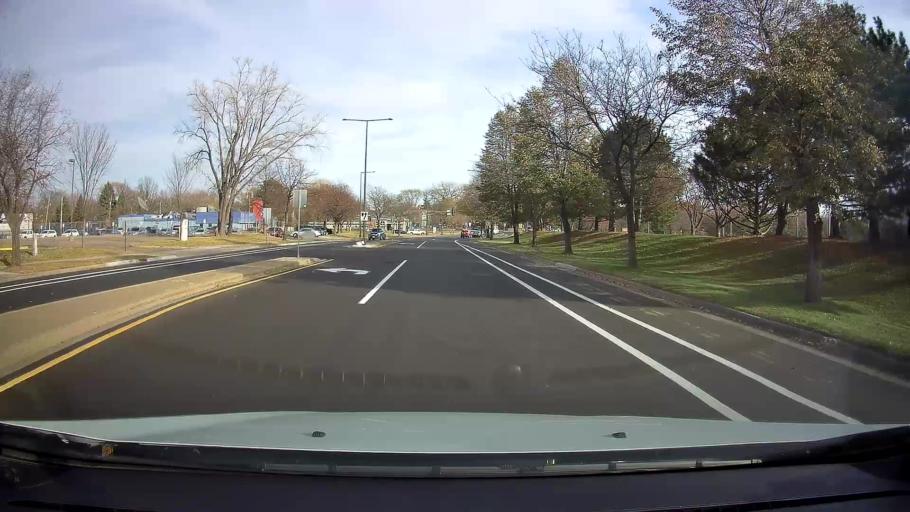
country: US
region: Minnesota
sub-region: Ramsey County
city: Falcon Heights
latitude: 44.9707
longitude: -93.1486
